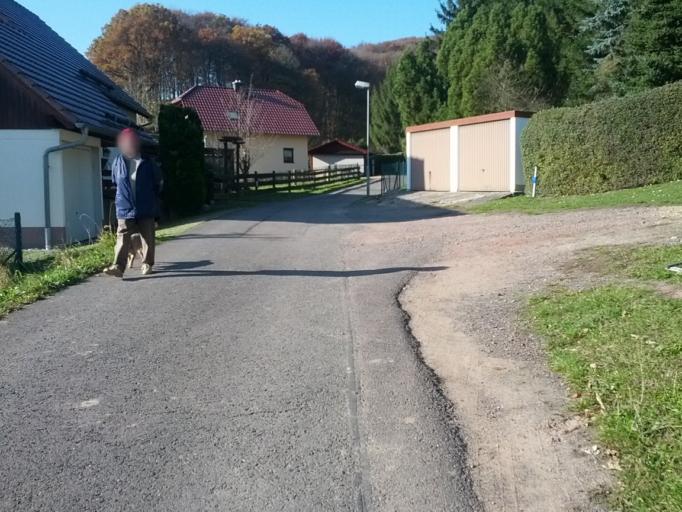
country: DE
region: Thuringia
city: Thal
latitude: 50.9260
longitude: 10.3842
